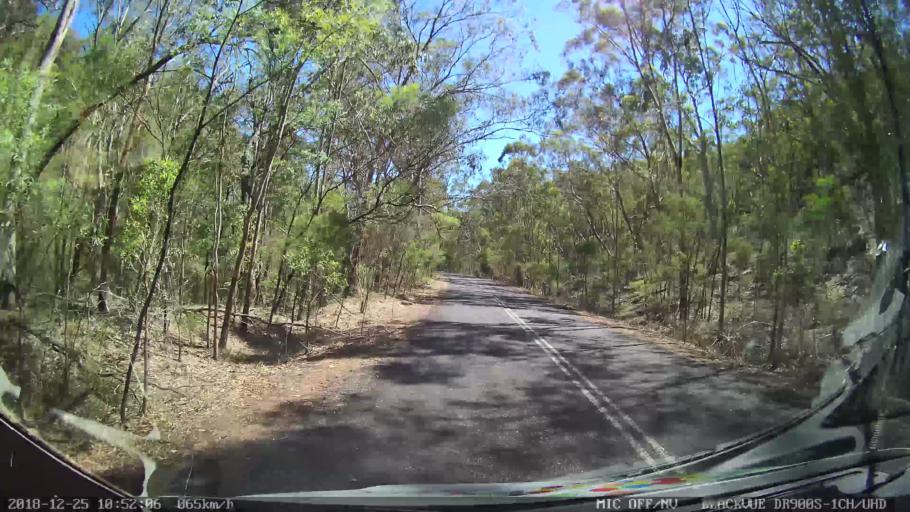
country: AU
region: New South Wales
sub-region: Upper Hunter Shire
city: Merriwa
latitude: -32.4317
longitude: 150.2731
